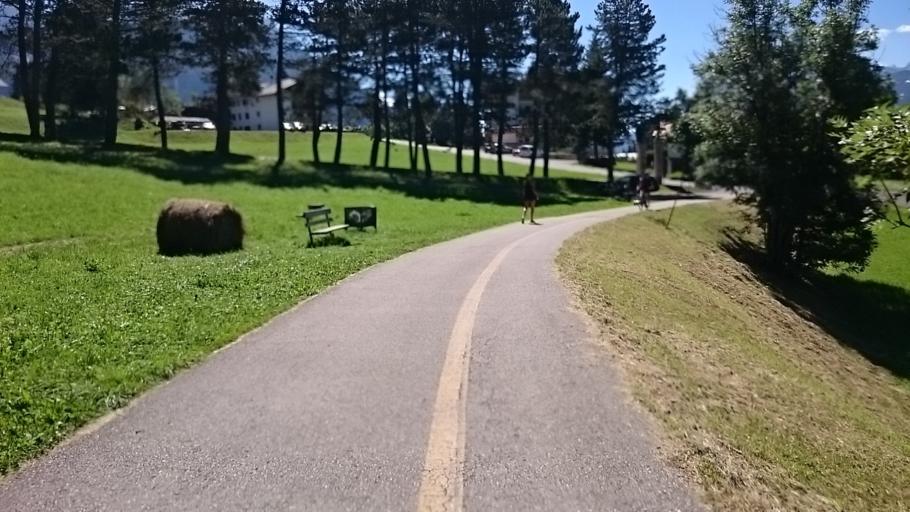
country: IT
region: Veneto
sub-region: Provincia di Belluno
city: Cortina d'Ampezzo
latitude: 46.5538
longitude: 12.1307
